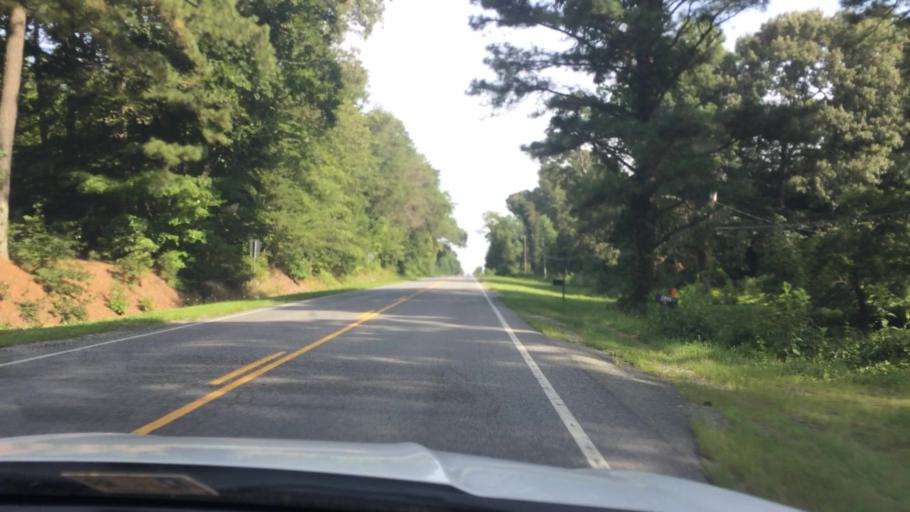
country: US
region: Virginia
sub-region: Northumberland County
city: Heathsville
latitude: 37.8711
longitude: -76.6211
